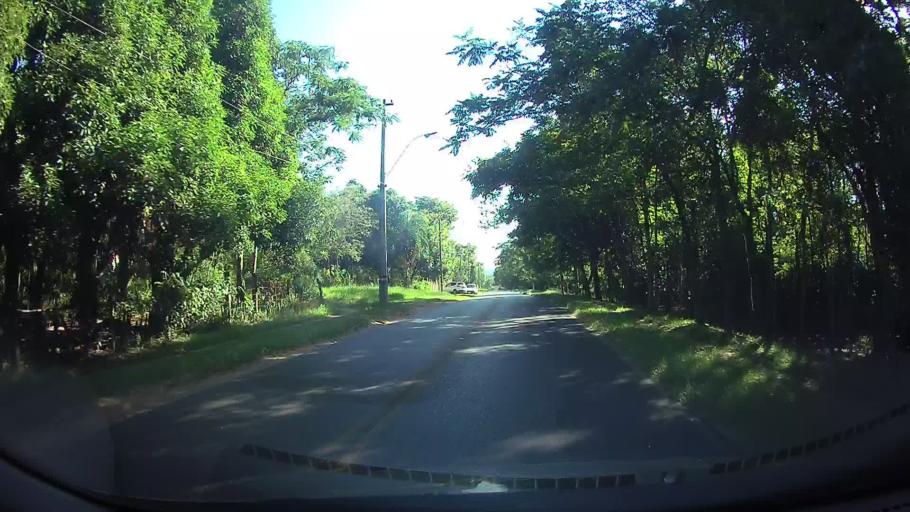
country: PY
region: Cordillera
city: Atyra
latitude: -25.2903
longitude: -57.1808
